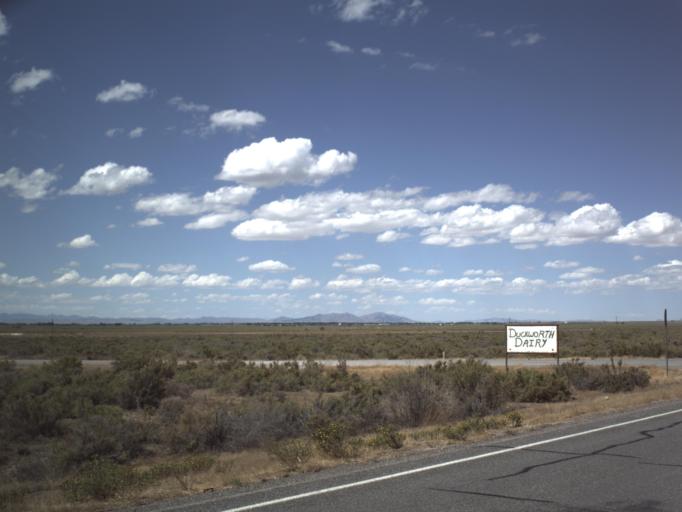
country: US
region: Utah
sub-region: Millard County
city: Delta
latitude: 39.3098
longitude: -112.4764
